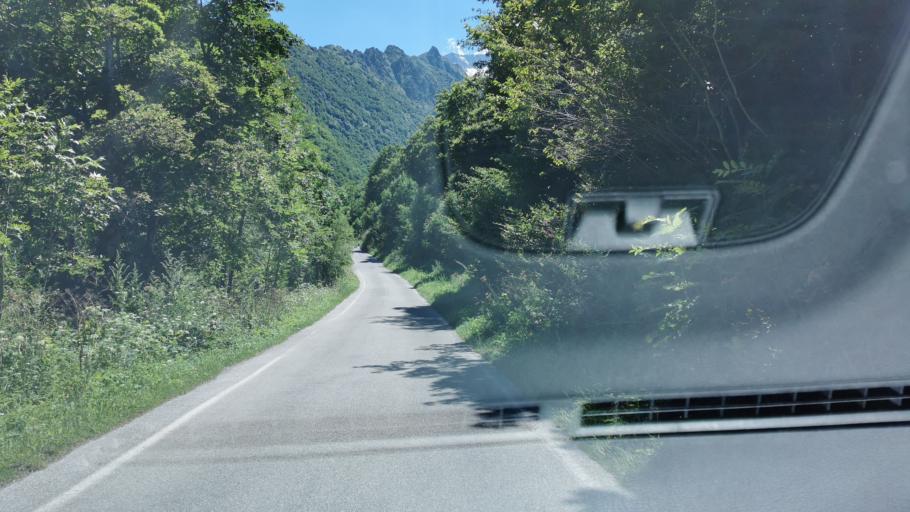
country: IT
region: Piedmont
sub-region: Provincia di Cuneo
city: Entracque
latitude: 44.1793
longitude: 7.3849
